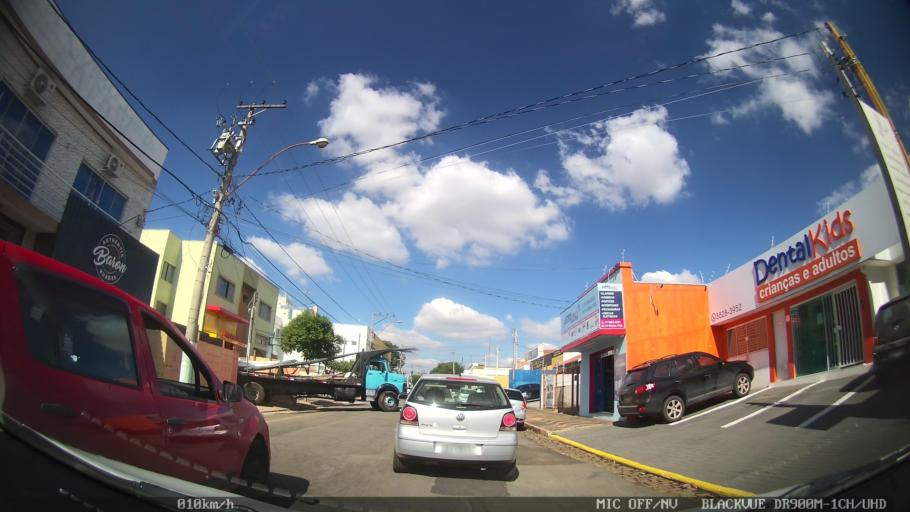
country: BR
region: Sao Paulo
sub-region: Sumare
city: Sumare
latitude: -22.8174
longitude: -47.2709
